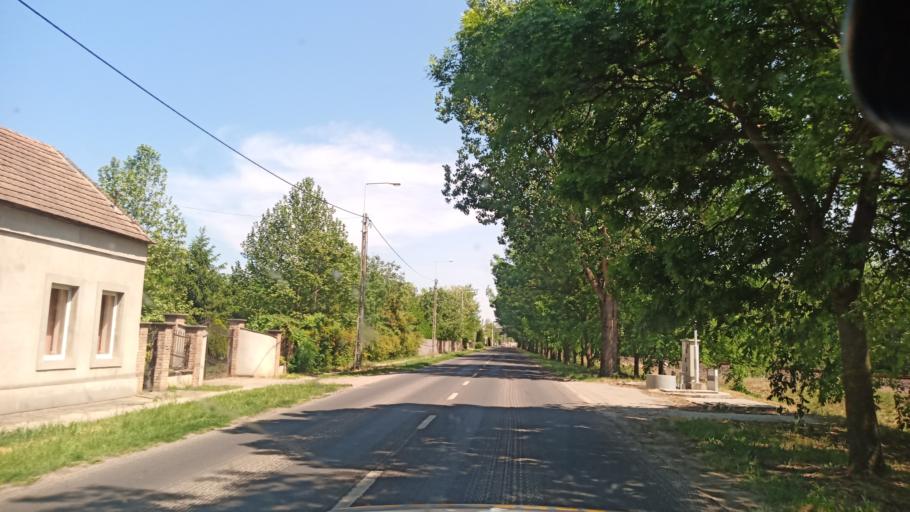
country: HU
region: Bekes
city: Oroshaza
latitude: 46.5592
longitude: 20.6422
